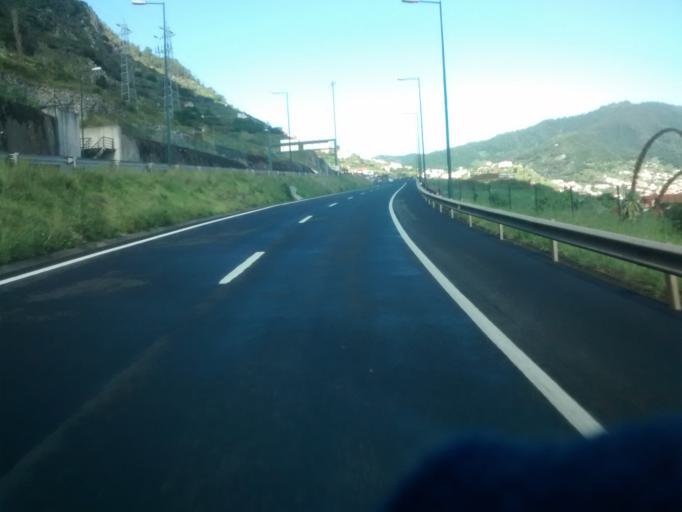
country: PT
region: Madeira
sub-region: Machico
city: Machico
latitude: 32.7175
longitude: -16.7704
